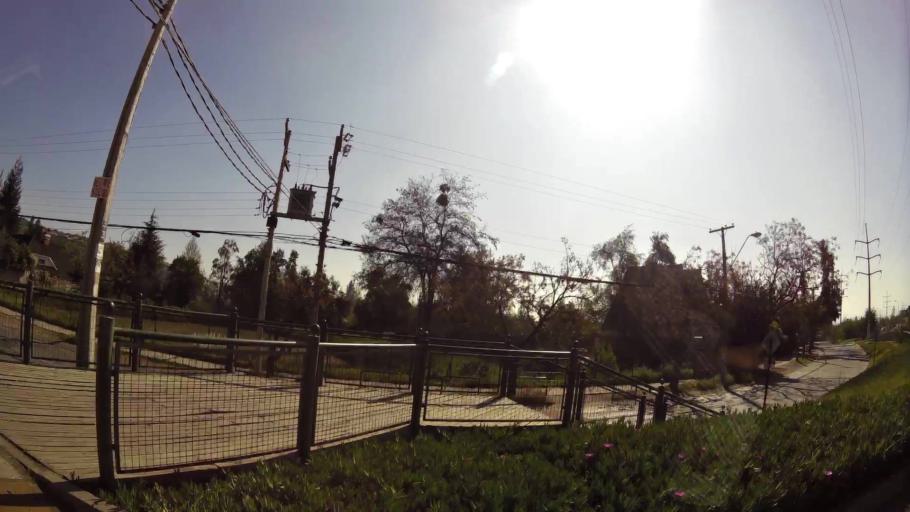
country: CL
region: Santiago Metropolitan
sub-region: Provincia de Santiago
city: Villa Presidente Frei, Nunoa, Santiago, Chile
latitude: -33.4133
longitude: -70.5126
